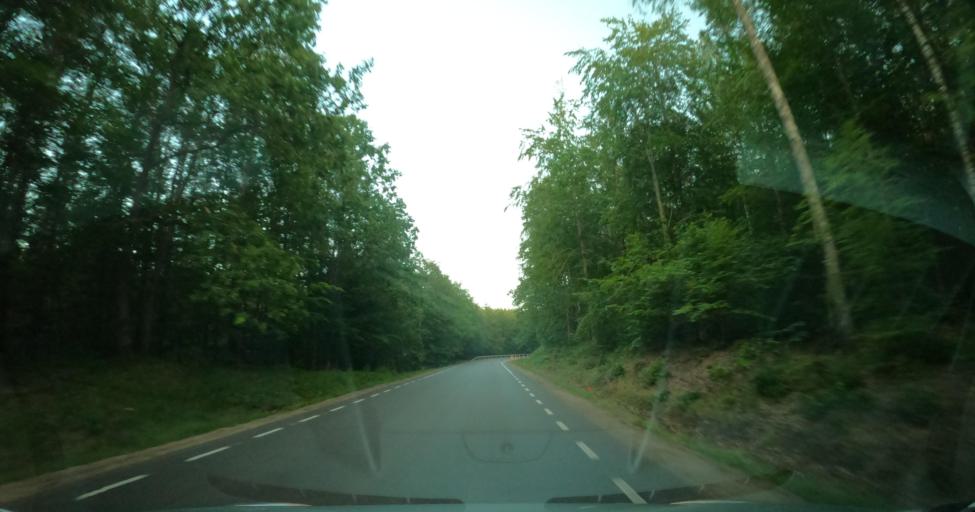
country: PL
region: Pomeranian Voivodeship
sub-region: Powiat leborski
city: Lebork
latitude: 54.5141
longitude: 17.8011
